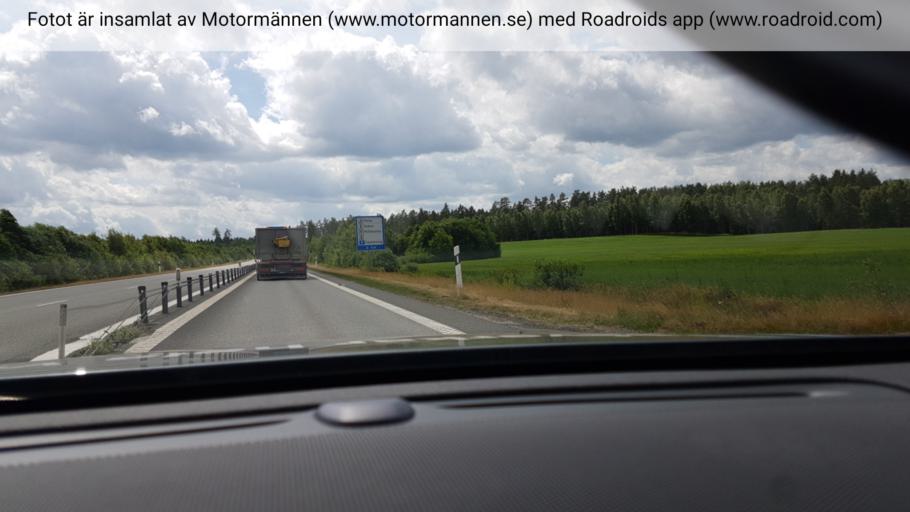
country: SE
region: Skane
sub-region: Hassleholms Kommun
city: Hassleholm
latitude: 56.1800
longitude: 13.8429
